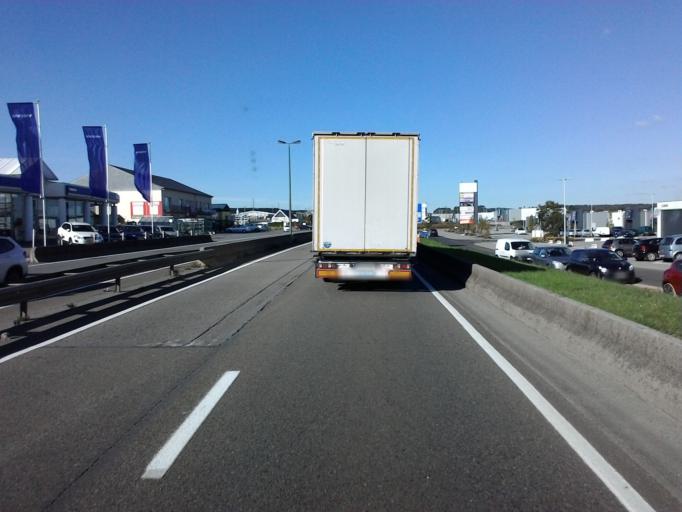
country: BE
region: Wallonia
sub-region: Province du Luxembourg
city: Messancy
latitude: 49.6223
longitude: 5.8100
